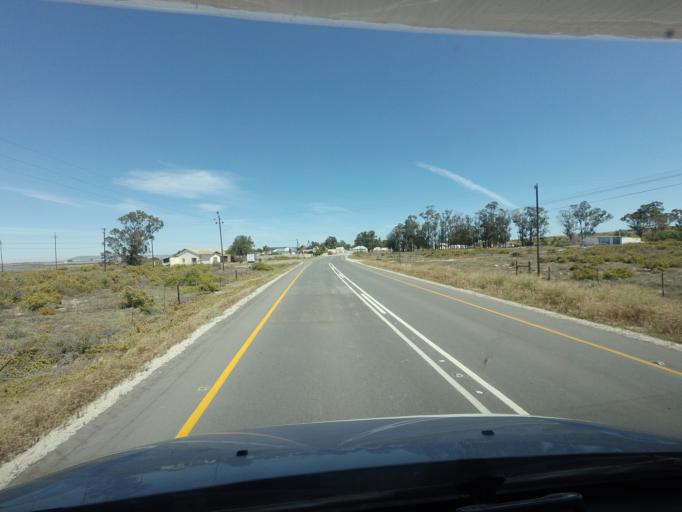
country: ZA
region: Western Cape
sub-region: West Coast District Municipality
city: Vredenburg
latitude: -32.7910
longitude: 18.2080
